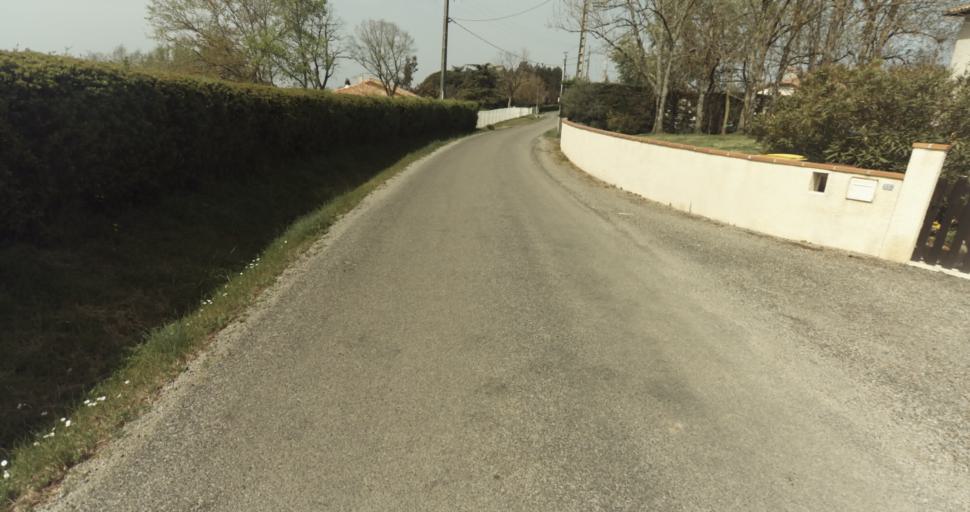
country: FR
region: Midi-Pyrenees
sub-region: Departement du Tarn-et-Garonne
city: Moissac
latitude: 44.1069
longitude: 1.0770
